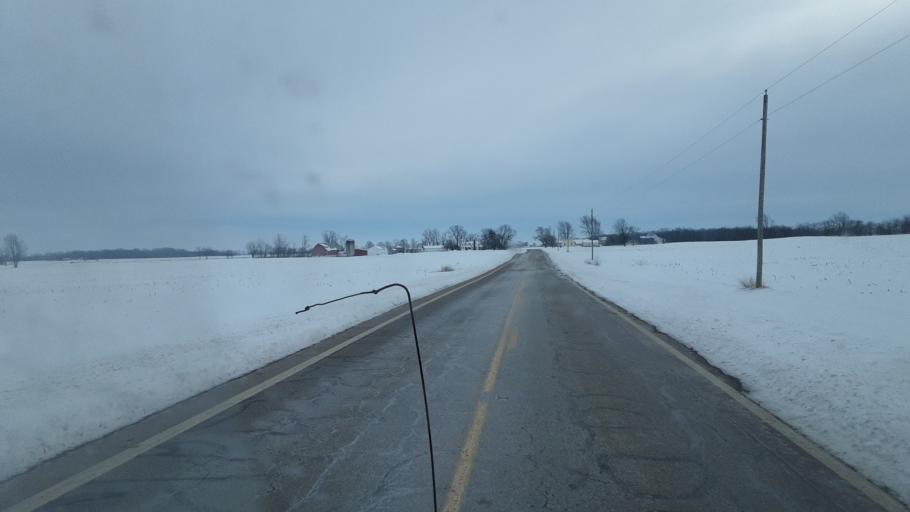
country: US
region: Ohio
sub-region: Champaign County
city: Mechanicsburg
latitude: 40.0316
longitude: -83.5303
